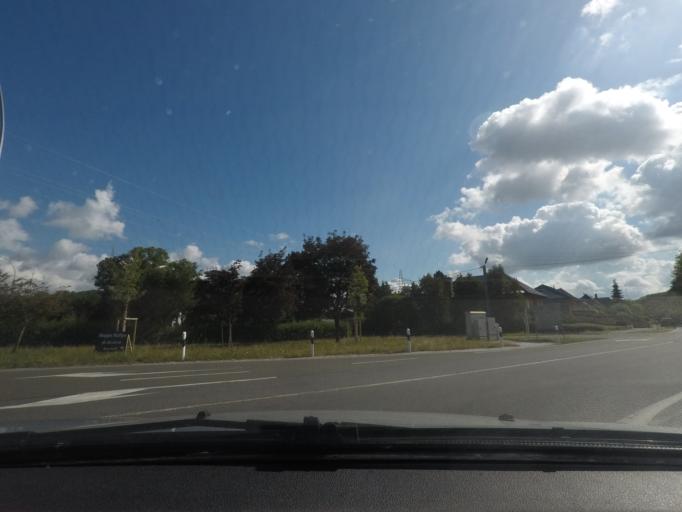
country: LU
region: Grevenmacher
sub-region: Canton de Grevenmacher
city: Junglinster
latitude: 49.7348
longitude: 6.2867
